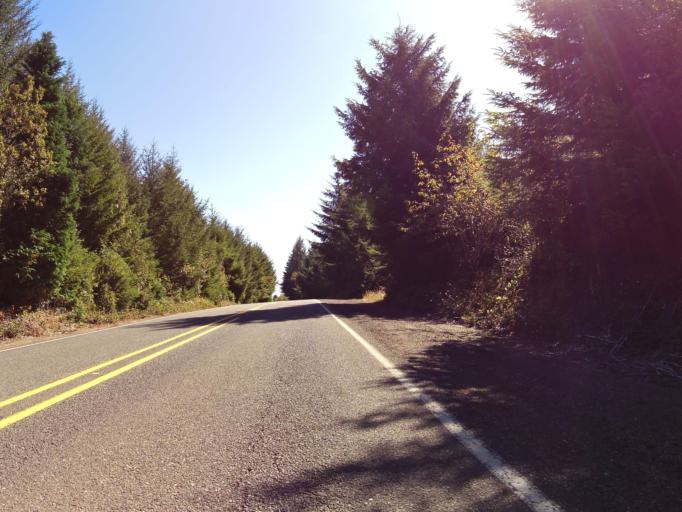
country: US
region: Oregon
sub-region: Coos County
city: Barview
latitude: 43.2641
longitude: -124.3438
